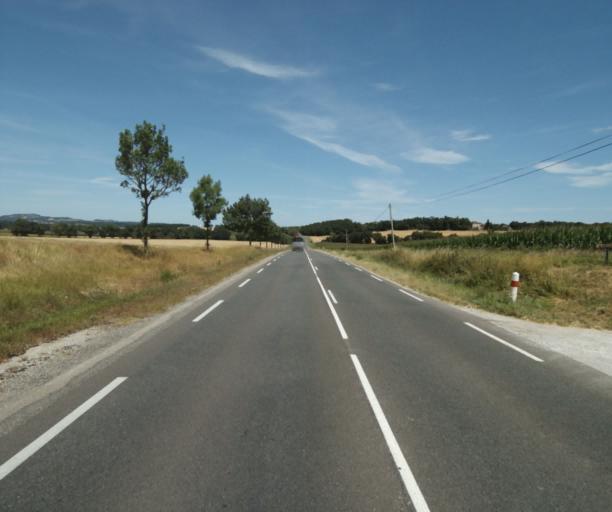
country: FR
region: Midi-Pyrenees
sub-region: Departement de la Haute-Garonne
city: Revel
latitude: 43.4905
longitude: 2.0376
